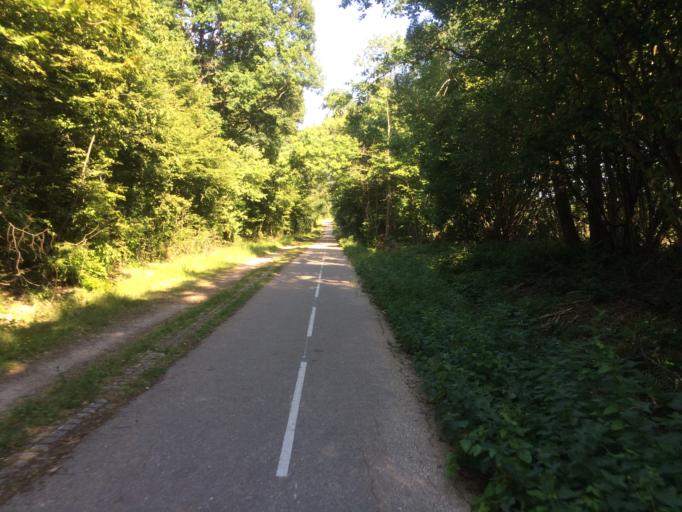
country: FR
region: Ile-de-France
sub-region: Departement du Val-de-Marne
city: Sucy-en-Brie
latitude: 48.7473
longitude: 2.5523
